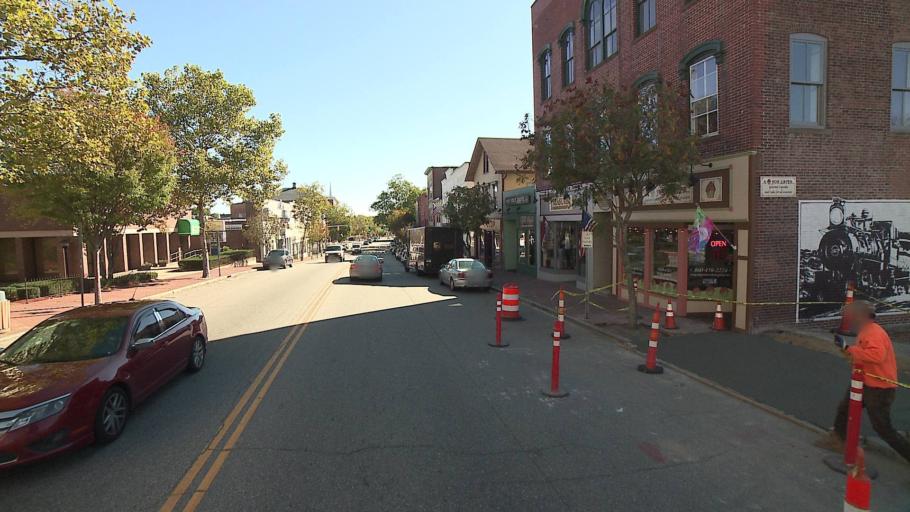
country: US
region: Connecticut
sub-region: Windham County
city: Willimantic
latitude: 41.7122
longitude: -72.2140
